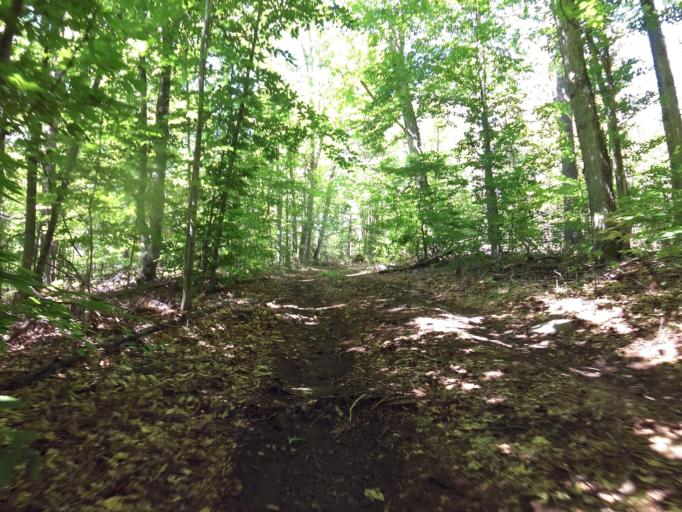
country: CA
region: Ontario
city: Renfrew
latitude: 45.1367
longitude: -76.5986
